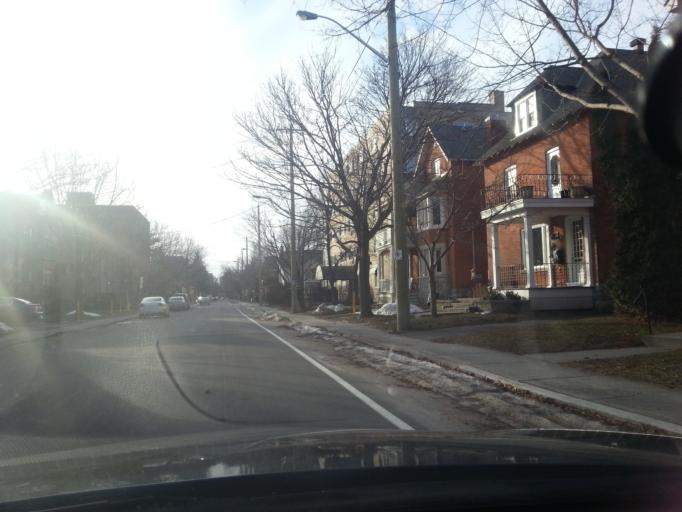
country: CA
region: Ontario
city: Ottawa
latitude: 45.4294
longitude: -75.6784
